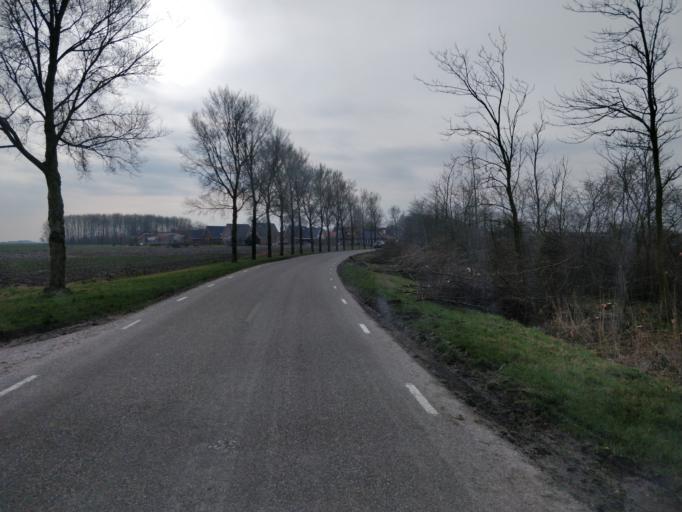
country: NL
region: Friesland
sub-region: Gemeente Dongeradeel
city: Holwerd
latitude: 53.3546
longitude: 5.9351
